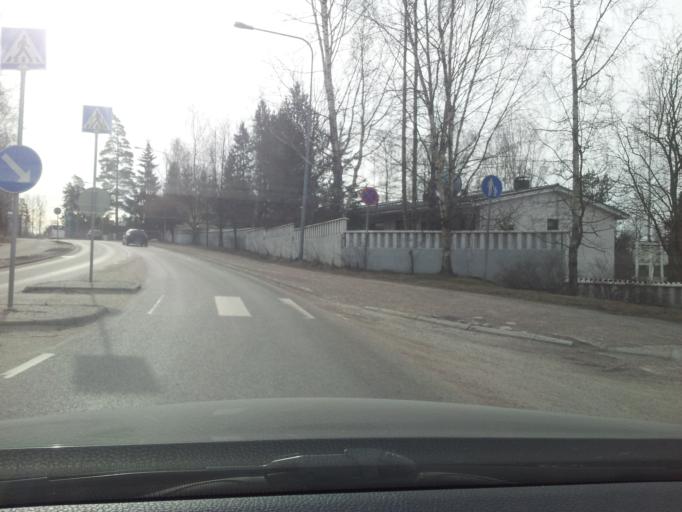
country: FI
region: Uusimaa
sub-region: Helsinki
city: Kilo
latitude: 60.1881
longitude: 24.7822
